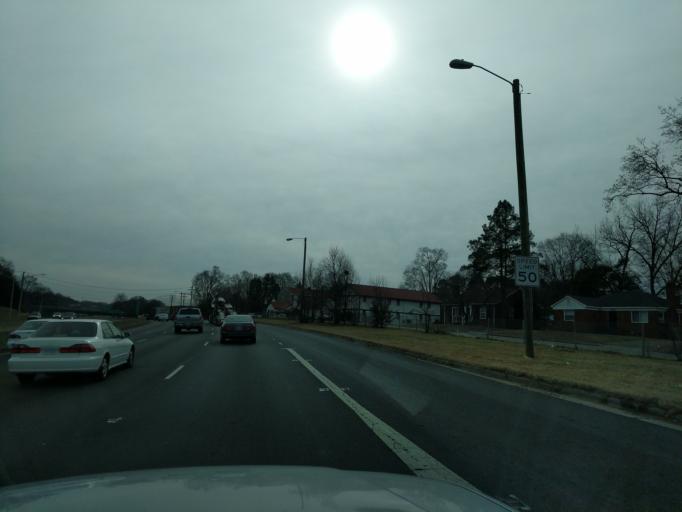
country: US
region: North Carolina
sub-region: Mecklenburg County
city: Charlotte
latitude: 35.2093
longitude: -80.8001
